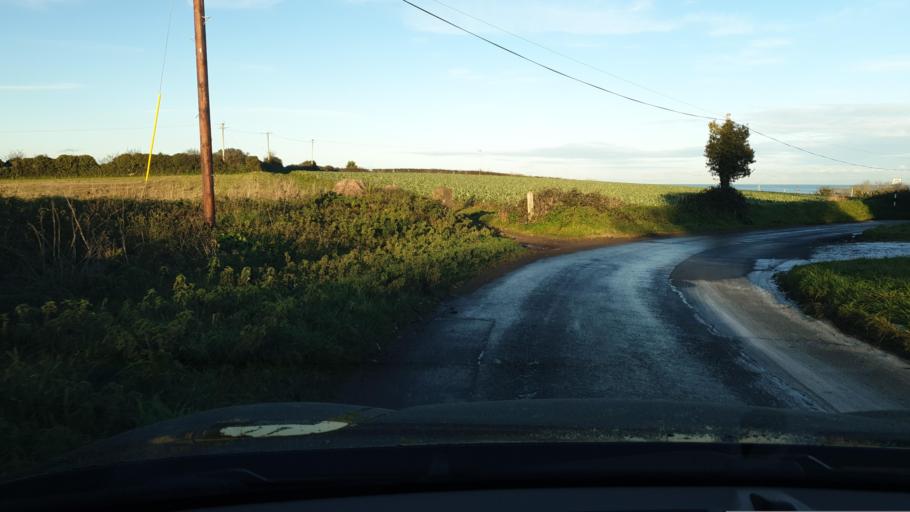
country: IE
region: Leinster
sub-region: Fingal County
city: Skerries
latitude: 53.5636
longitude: -6.1181
